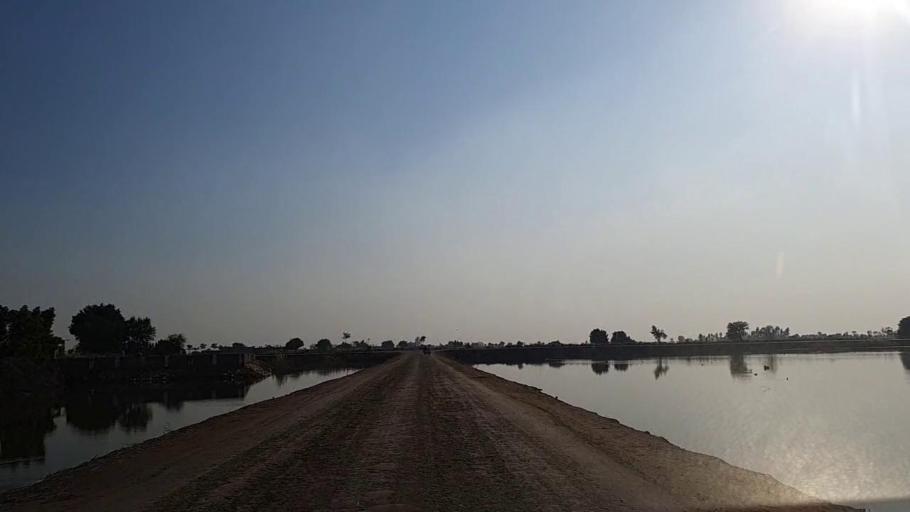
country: PK
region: Sindh
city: Daur
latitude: 26.4058
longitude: 68.2743
